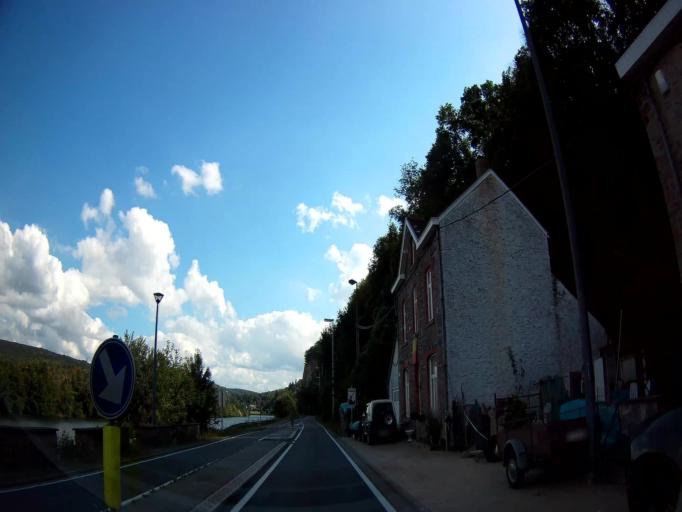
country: BE
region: Wallonia
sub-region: Province de Namur
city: Yvoir
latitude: 50.3444
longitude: 4.8552
